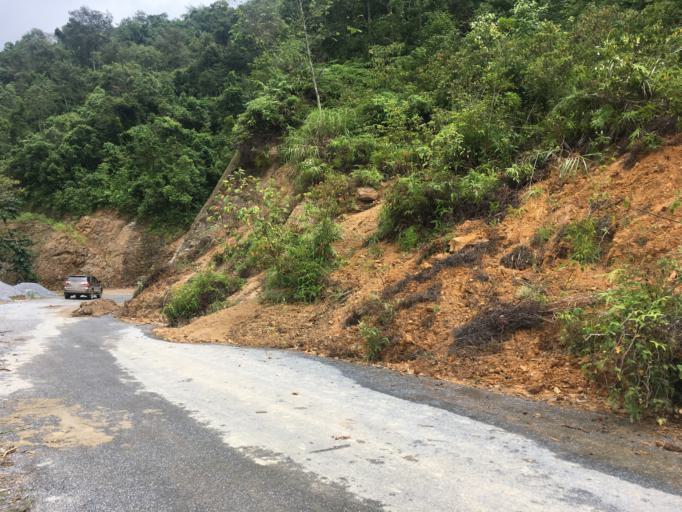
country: VN
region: Ha Giang
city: Thi Tran Tam Son
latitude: 22.9952
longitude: 105.0688
